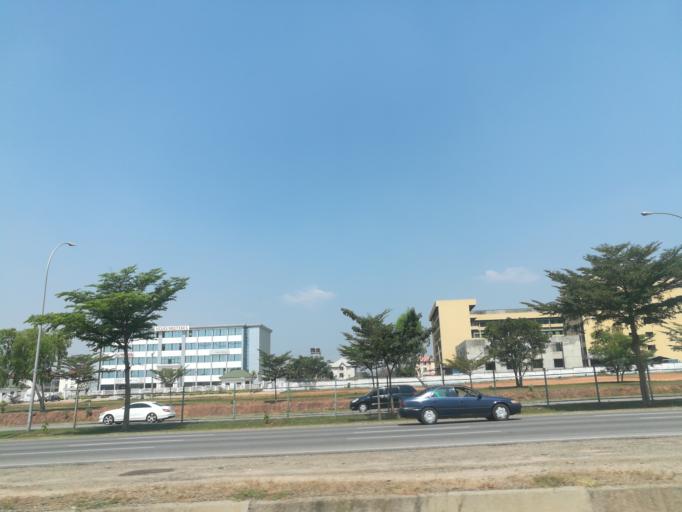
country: NG
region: Abuja Federal Capital Territory
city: Abuja
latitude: 9.0768
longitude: 7.4458
